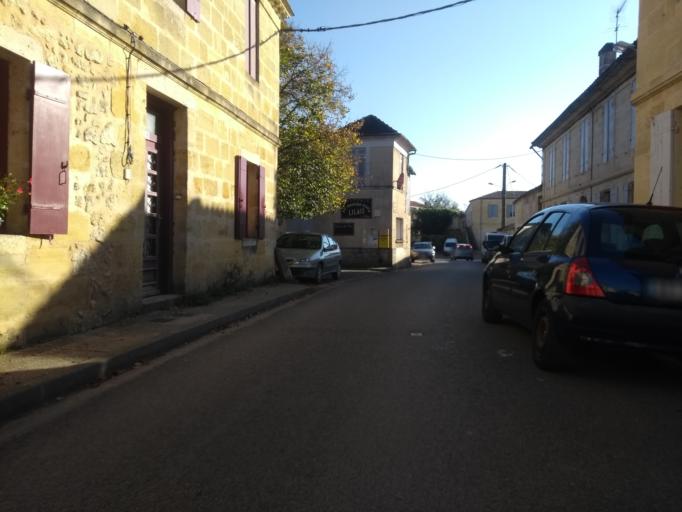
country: FR
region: Aquitaine
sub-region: Departement de la Gironde
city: Cambes
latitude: 44.7253
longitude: -0.4743
